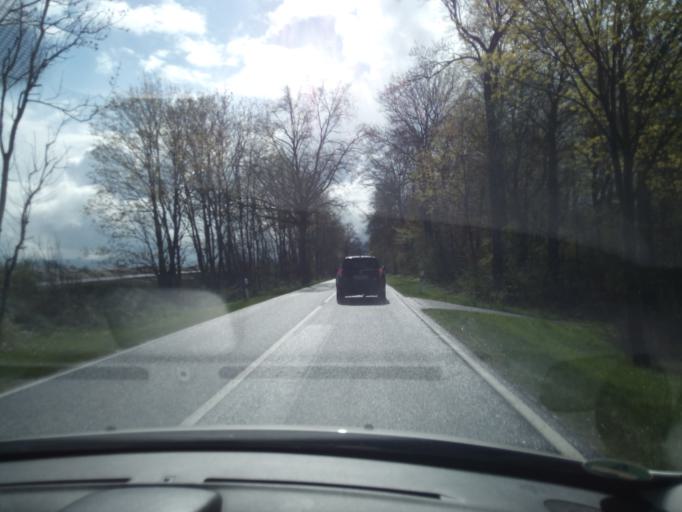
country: DE
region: Mecklenburg-Vorpommern
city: Loitz
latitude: 53.3781
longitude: 13.3528
